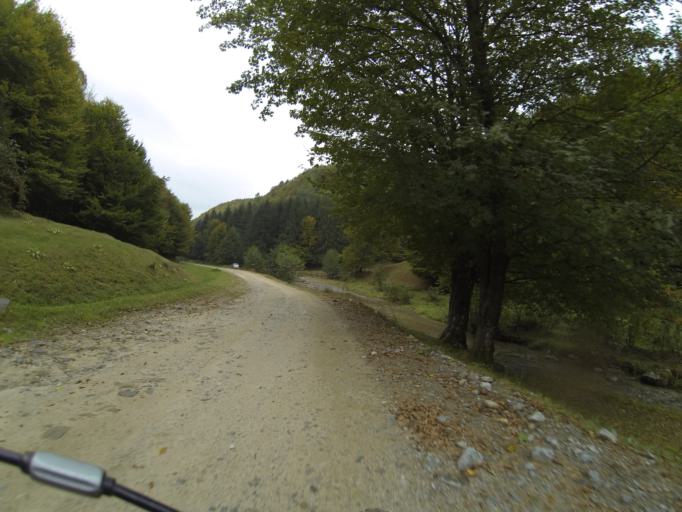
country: RO
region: Gorj
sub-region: Comuna Tismana
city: Sohodol
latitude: 45.0698
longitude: 22.8869
